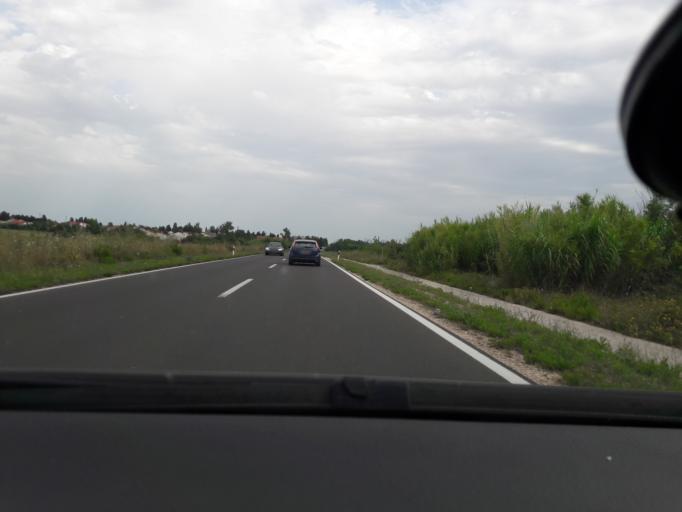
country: HR
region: Zadarska
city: Privlaka
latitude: 44.2592
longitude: 15.1510
